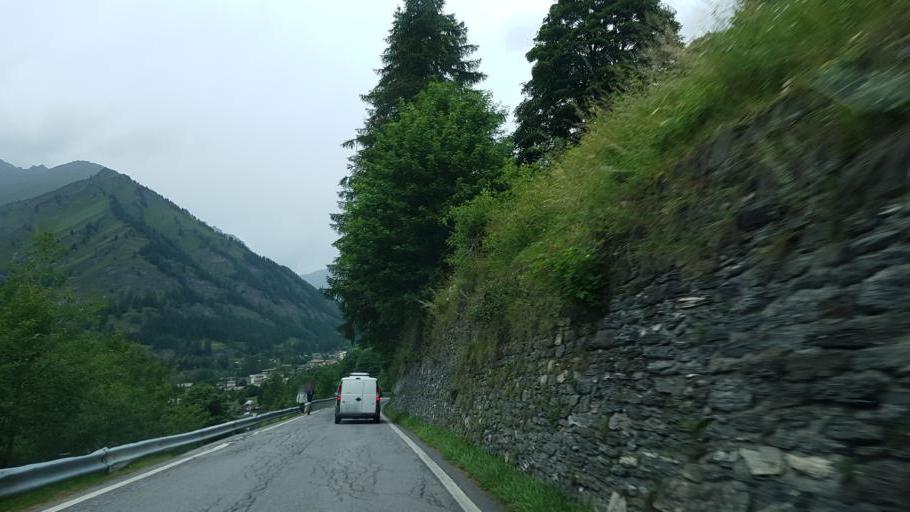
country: IT
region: Piedmont
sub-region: Provincia di Cuneo
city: Pontechianale
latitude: 44.6182
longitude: 7.0381
